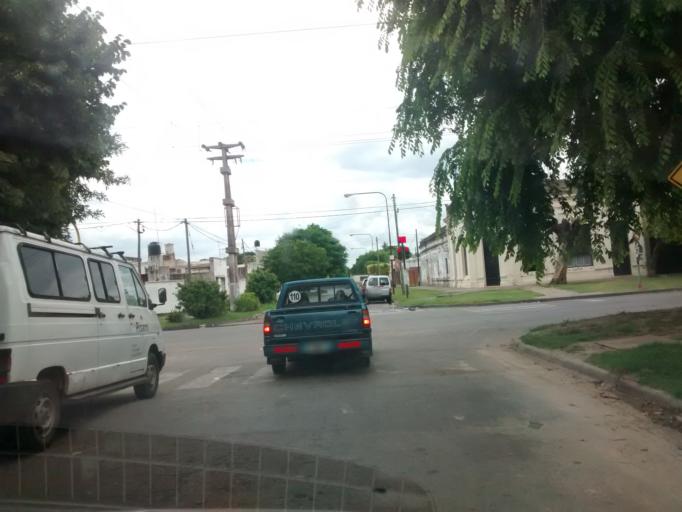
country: AR
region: Buenos Aires
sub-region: Partido de La Plata
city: La Plata
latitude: -34.9213
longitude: -57.9131
